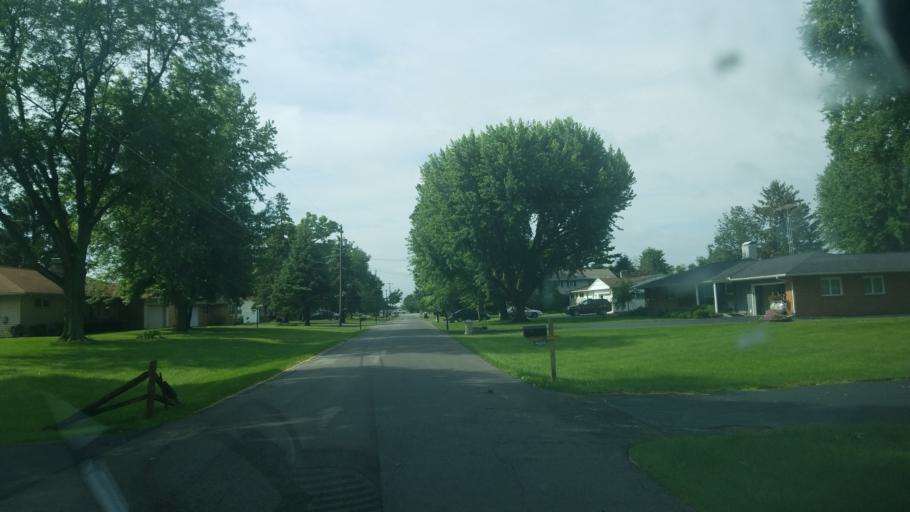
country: US
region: Ohio
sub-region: Marion County
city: Marion
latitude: 40.5668
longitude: -83.1090
